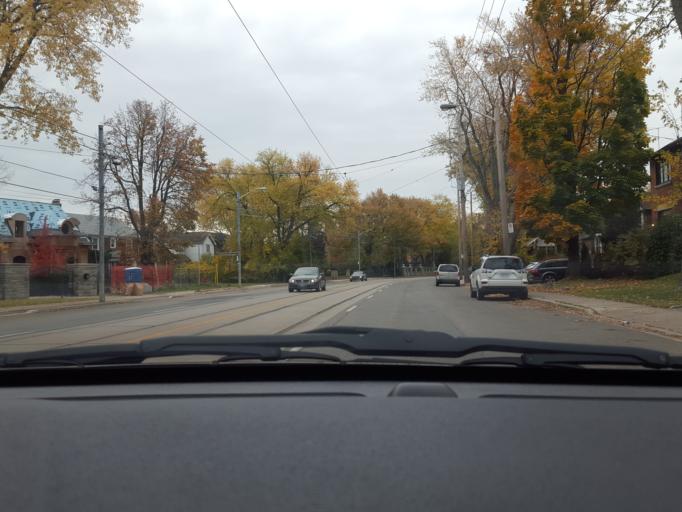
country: CA
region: Ontario
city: Etobicoke
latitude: 43.6060
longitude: -79.4910
